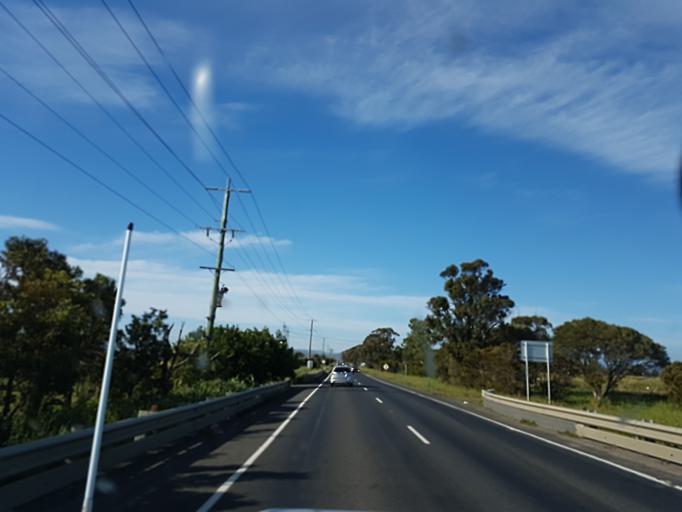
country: AU
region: Victoria
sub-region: Cardinia
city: Pakenham South
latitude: -38.1143
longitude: 145.4855
